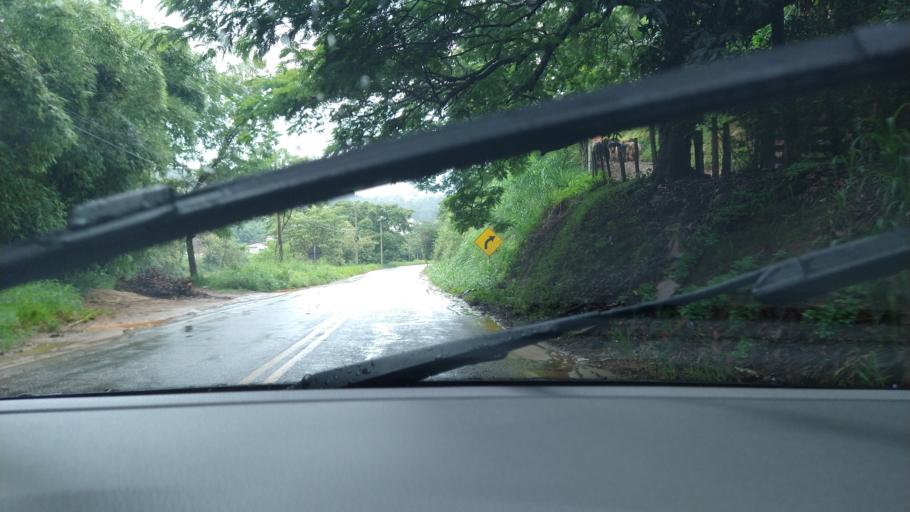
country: BR
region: Minas Gerais
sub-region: Ponte Nova
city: Ponte Nova
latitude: -20.3829
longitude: -42.9020
